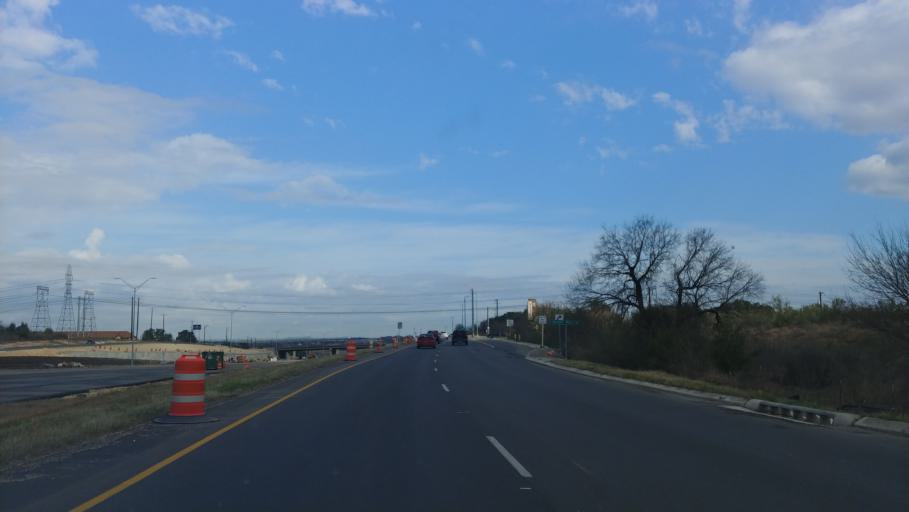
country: US
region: Texas
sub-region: Bexar County
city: Lackland Air Force Base
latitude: 29.4121
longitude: -98.7093
